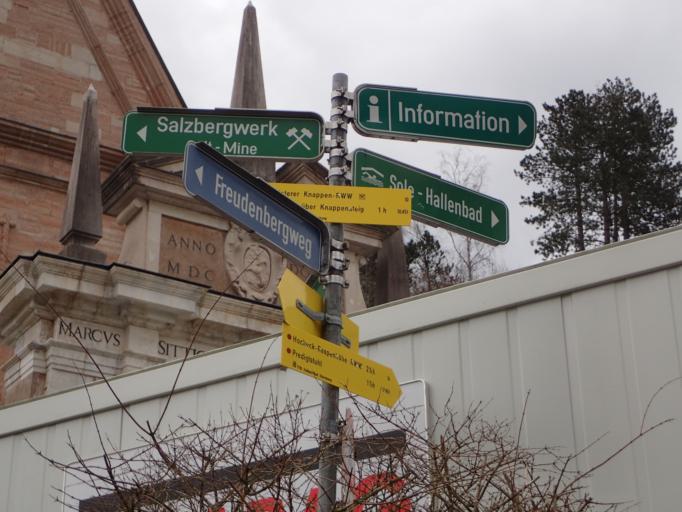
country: AT
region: Salzburg
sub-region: Politischer Bezirk Hallein
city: Hallein
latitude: 47.6653
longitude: 13.0894
